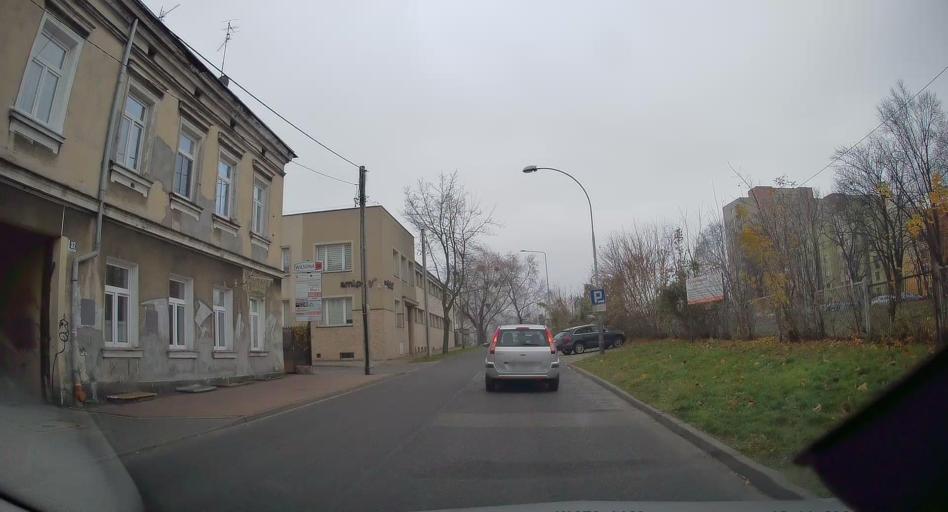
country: PL
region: Silesian Voivodeship
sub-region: Czestochowa
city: Czestochowa
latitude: 50.8157
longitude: 19.1221
